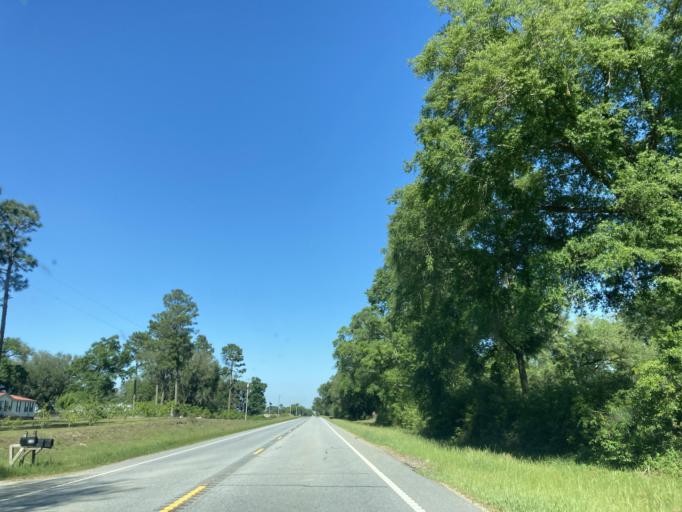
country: US
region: Georgia
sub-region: Baker County
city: Newton
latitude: 31.2583
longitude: -84.4127
